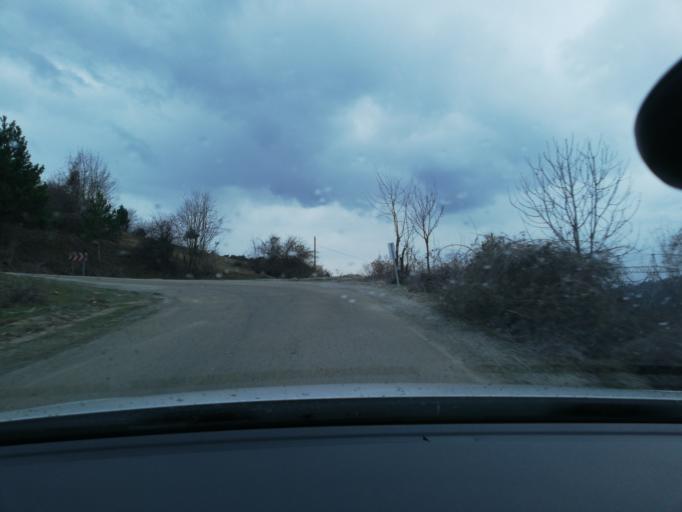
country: TR
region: Bolu
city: Gokcesu
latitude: 40.7365
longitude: 31.8346
